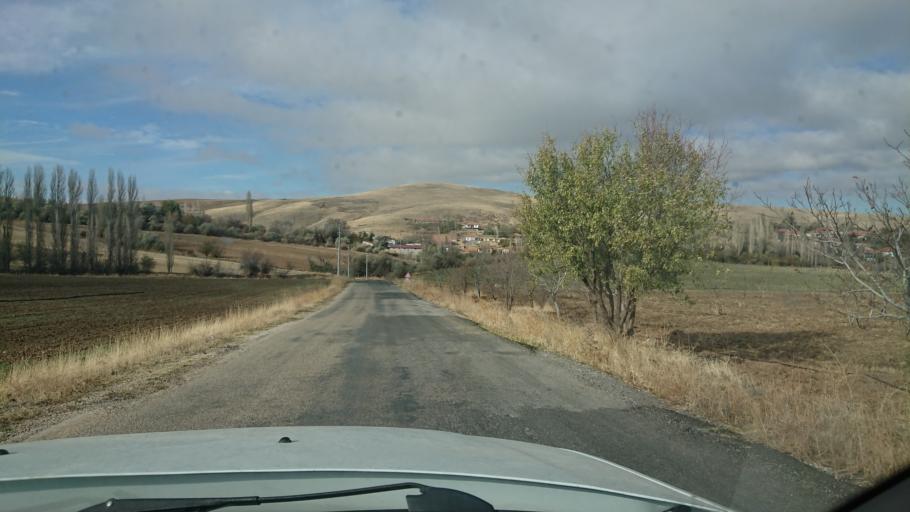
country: TR
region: Aksaray
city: Ortakoy
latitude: 38.8034
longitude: 33.9861
